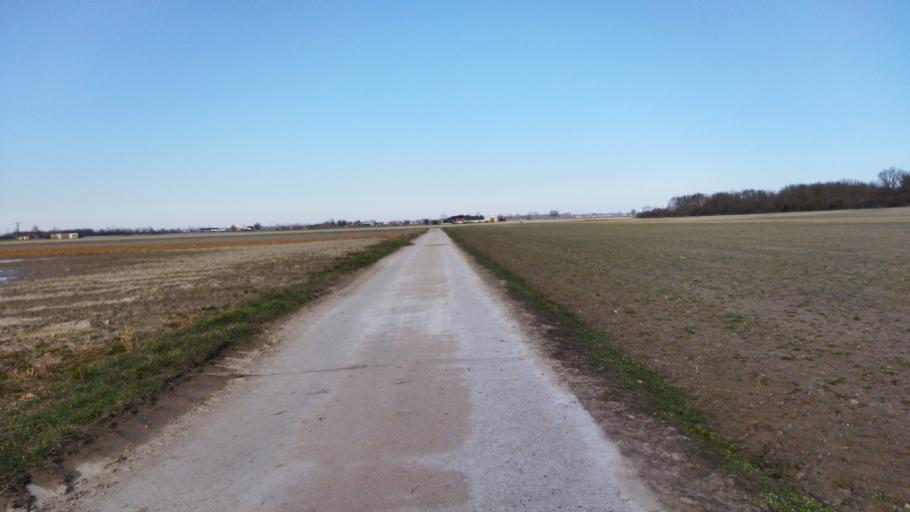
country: DE
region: Rheinland-Pfalz
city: Waldsee
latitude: 49.3793
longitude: 8.4282
